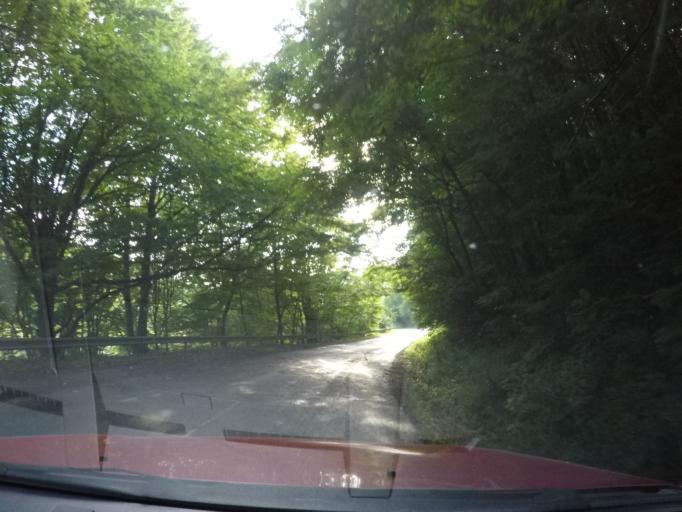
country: UA
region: Zakarpattia
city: Velykyi Bereznyi
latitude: 48.9410
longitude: 22.4898
